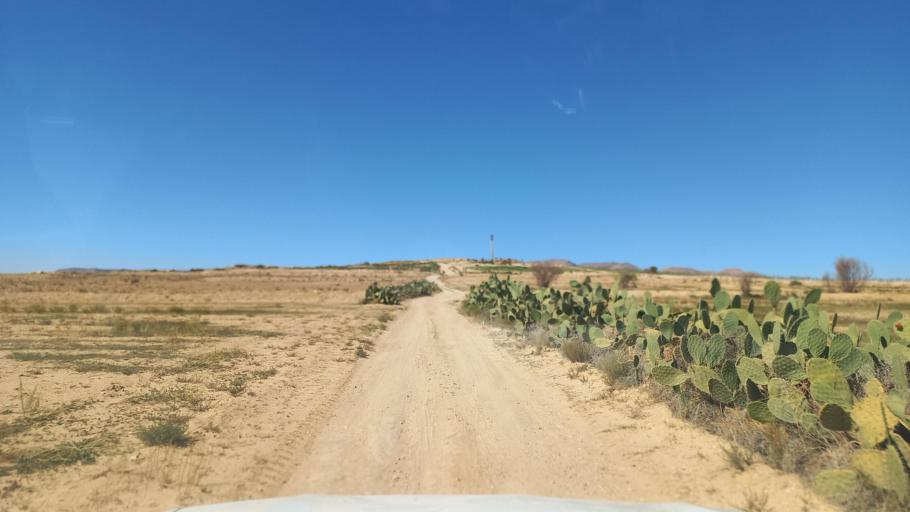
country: TN
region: Al Qasrayn
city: Sbiba
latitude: 35.3730
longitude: 9.0820
